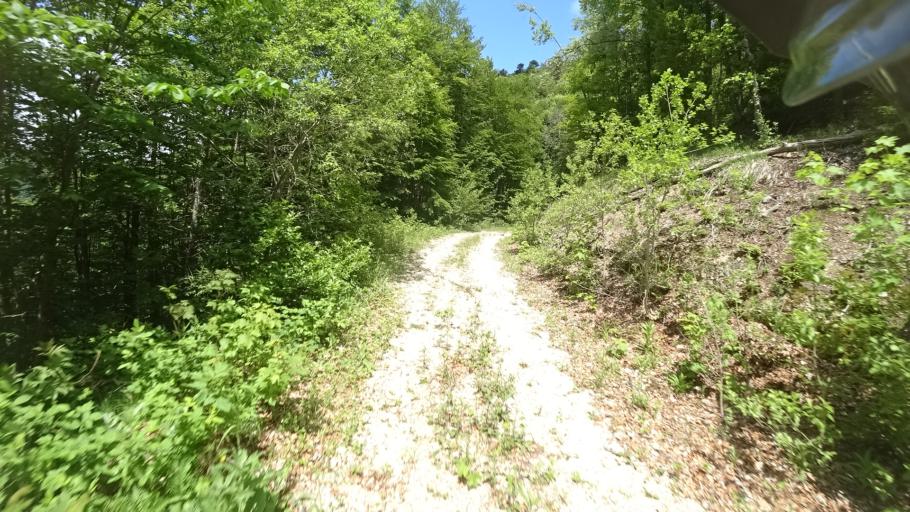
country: BA
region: Federation of Bosnia and Herzegovina
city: Orasac
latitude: 44.5654
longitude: 15.8667
